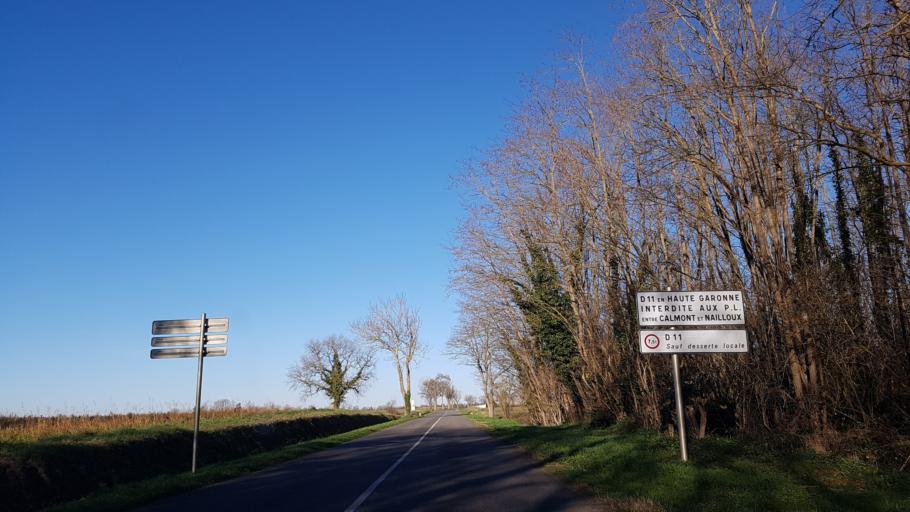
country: FR
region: Midi-Pyrenees
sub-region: Departement de l'Ariege
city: Mazeres
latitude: 43.2676
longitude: 1.6564
